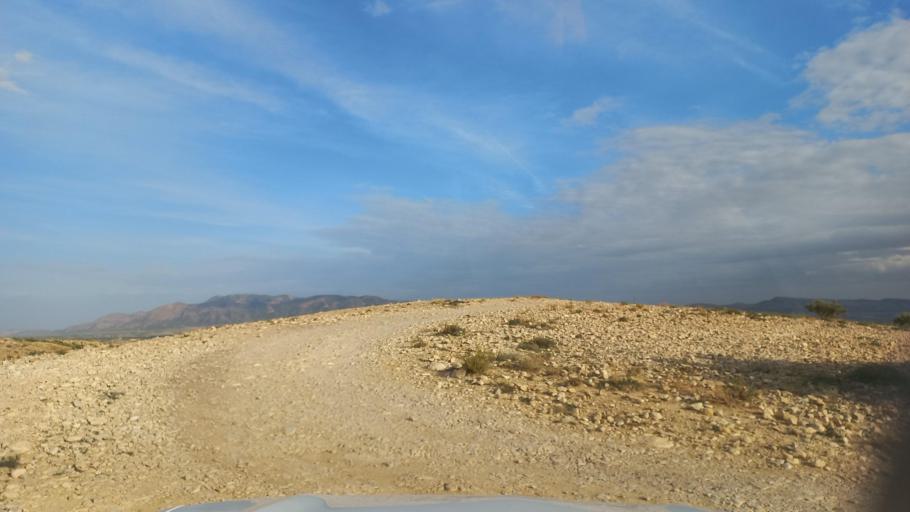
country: TN
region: Al Qasrayn
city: Sbiba
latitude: 35.4555
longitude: 9.0835
